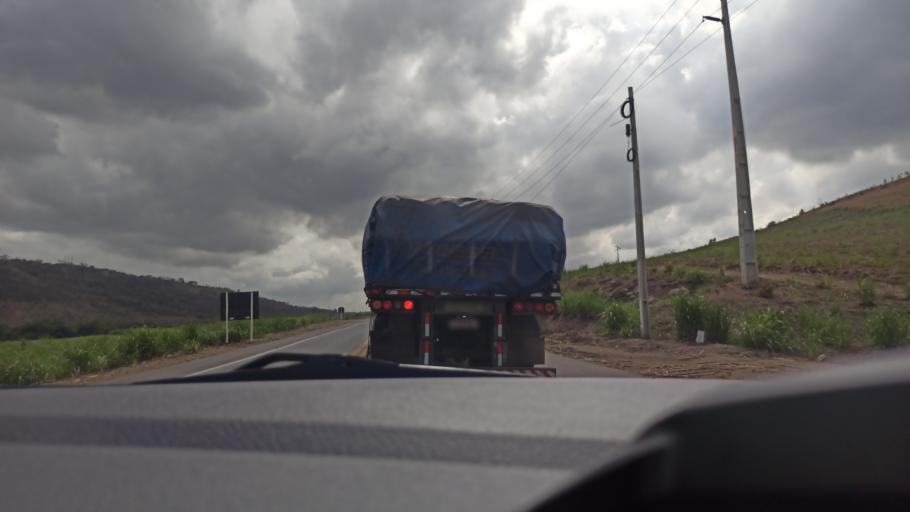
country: BR
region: Pernambuco
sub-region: Timbauba
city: Timbauba
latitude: -7.5226
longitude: -35.2970
